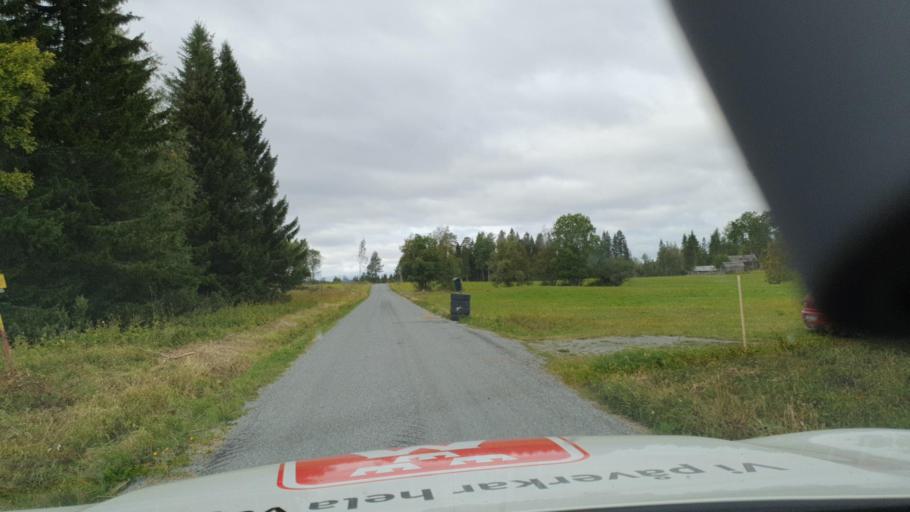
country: SE
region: Jaemtland
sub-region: OEstersunds Kommun
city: Ostersund
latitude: 63.1171
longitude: 14.6019
